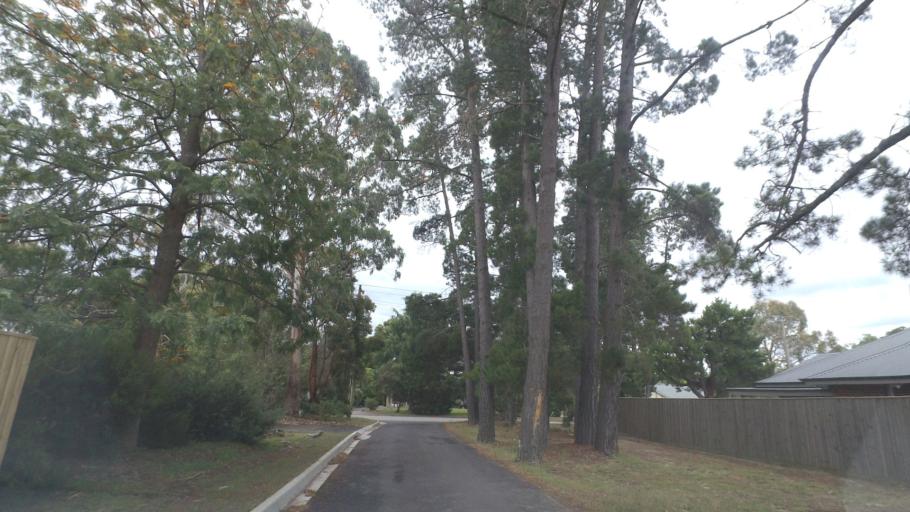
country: AU
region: Victoria
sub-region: Manningham
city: Park Orchards
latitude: -37.7787
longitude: 145.2236
